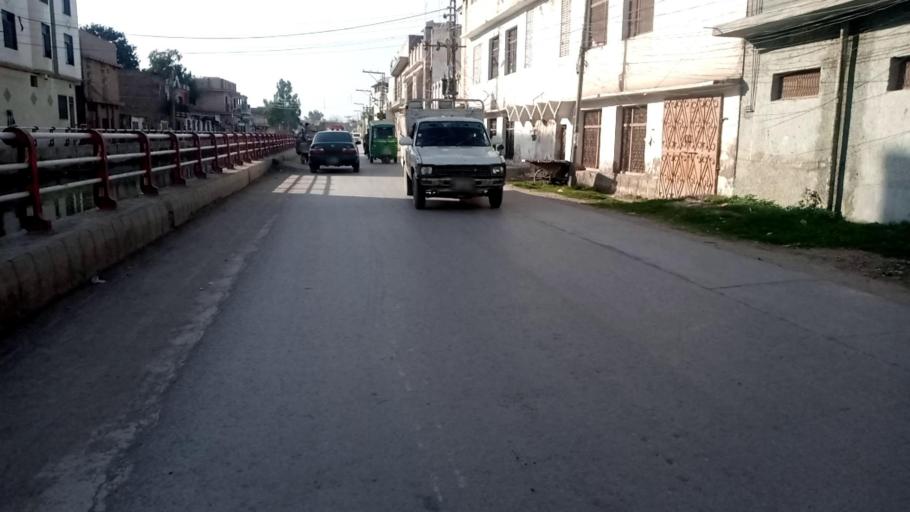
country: PK
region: Khyber Pakhtunkhwa
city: Peshawar
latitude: 34.0141
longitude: 71.6092
